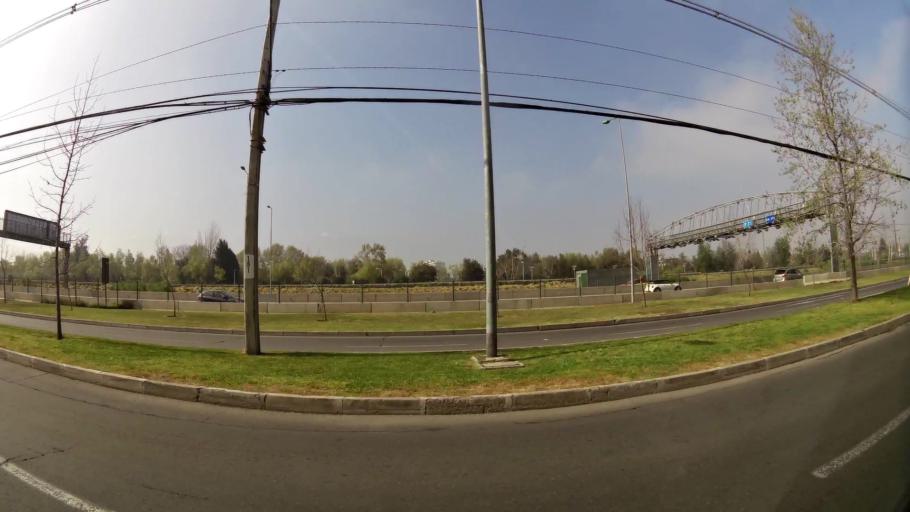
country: CL
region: Santiago Metropolitan
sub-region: Provincia de Santiago
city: Villa Presidente Frei, Nunoa, Santiago, Chile
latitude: -33.3842
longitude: -70.5927
